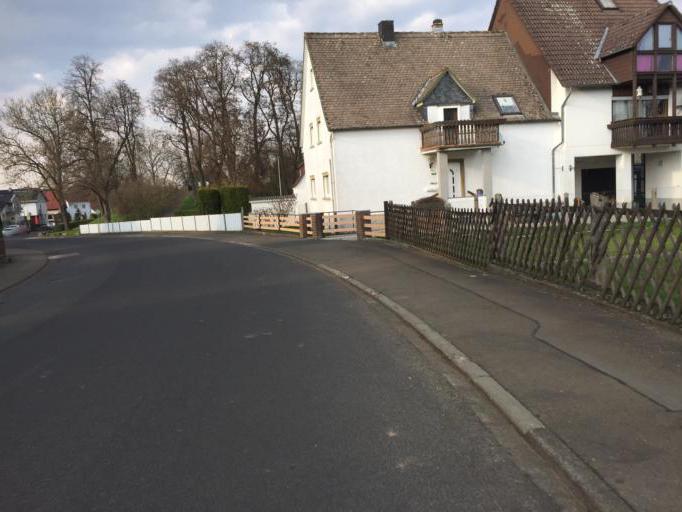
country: DE
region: Hesse
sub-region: Regierungsbezirk Giessen
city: Laubach
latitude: 50.5440
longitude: 8.9561
